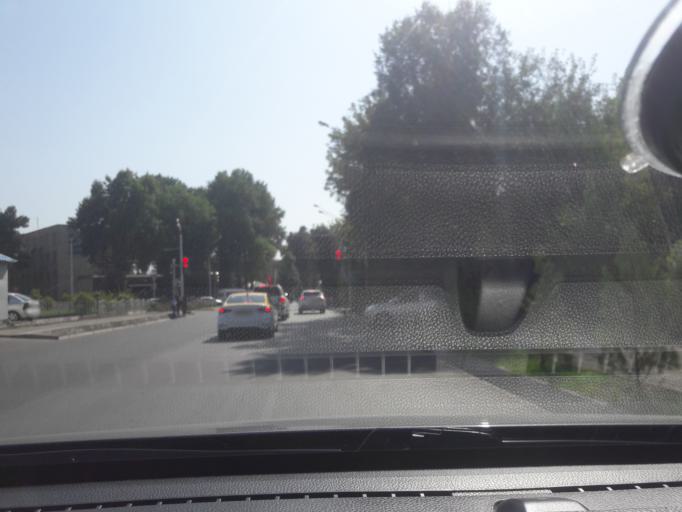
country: TJ
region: Dushanbe
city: Dushanbe
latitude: 38.5730
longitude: 68.8000
